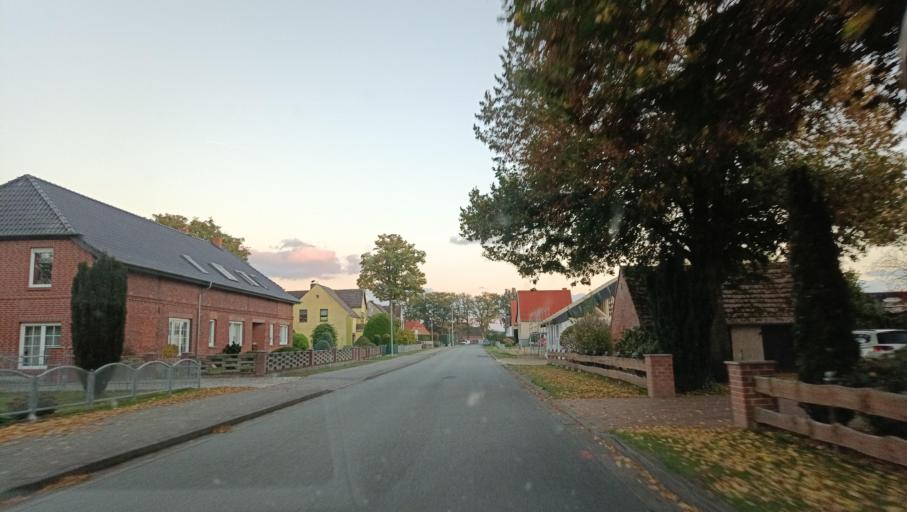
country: DE
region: Mecklenburg-Vorpommern
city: Ludwigslust
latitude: 53.2788
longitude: 11.4944
